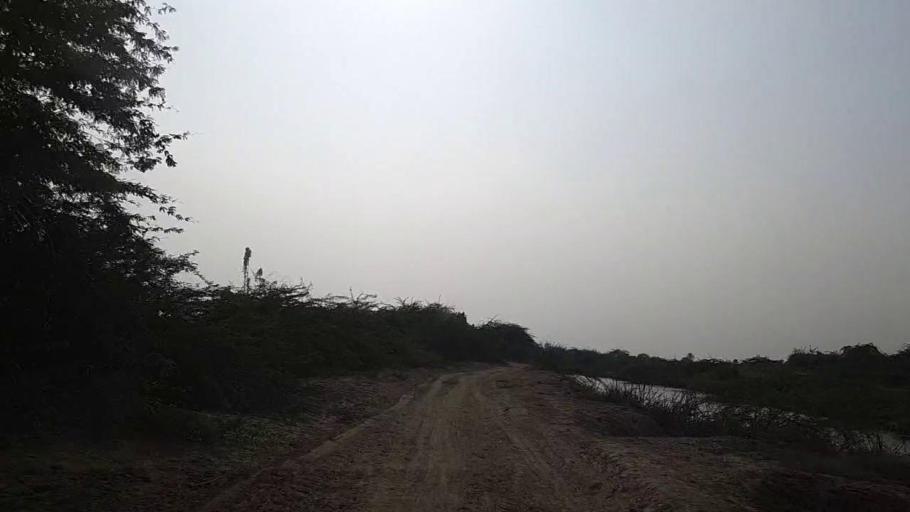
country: PK
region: Sindh
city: Gharo
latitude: 24.6565
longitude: 67.6211
